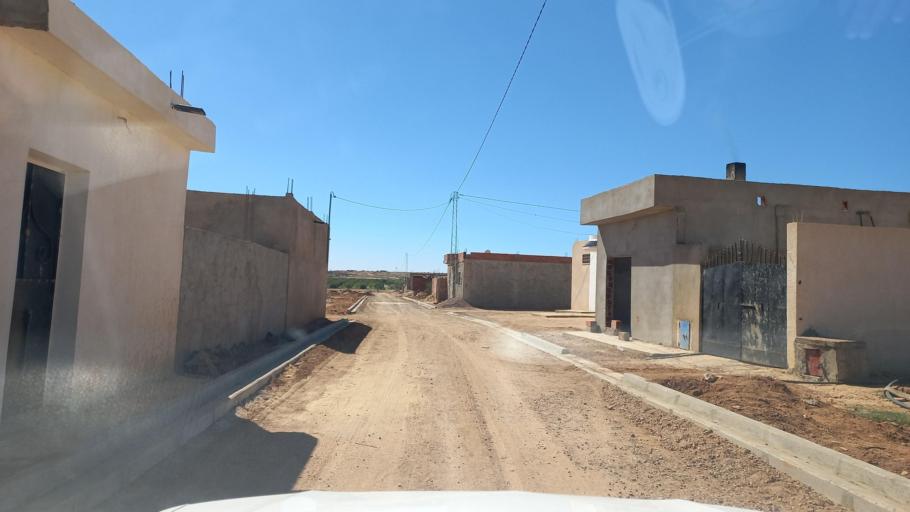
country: TN
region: Al Qasrayn
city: Sbiba
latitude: 35.3601
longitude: 9.0896
